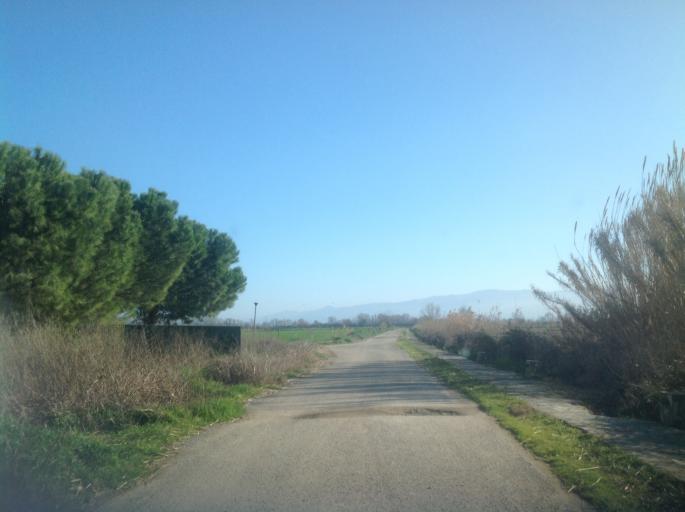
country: IT
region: Calabria
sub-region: Provincia di Cosenza
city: Sibari
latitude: 39.7218
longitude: 16.4952
